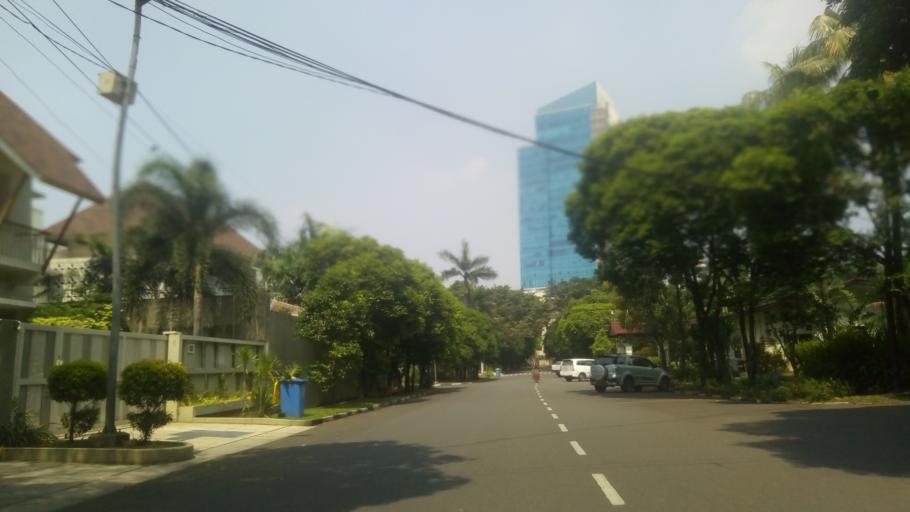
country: ID
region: Jakarta Raya
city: Jakarta
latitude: -6.2372
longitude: 106.8346
